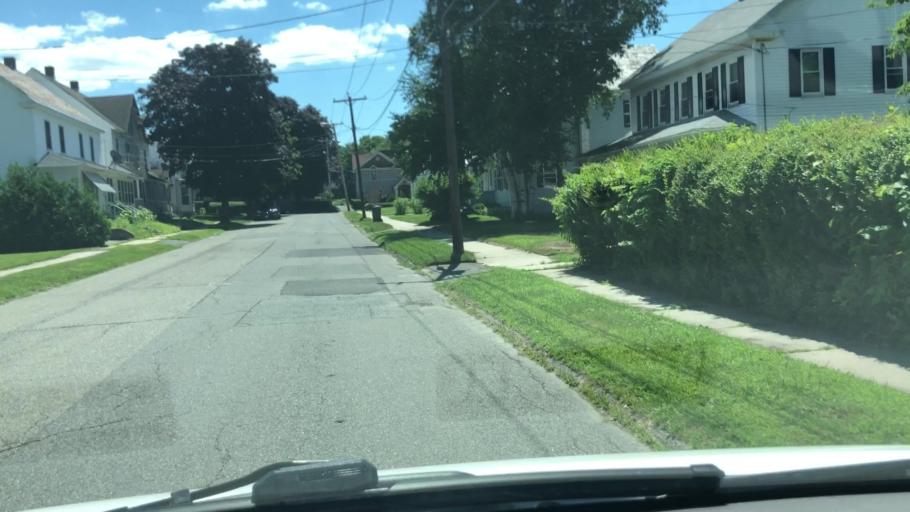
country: US
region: Massachusetts
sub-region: Berkshire County
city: Adams
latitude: 42.6260
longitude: -73.1152
